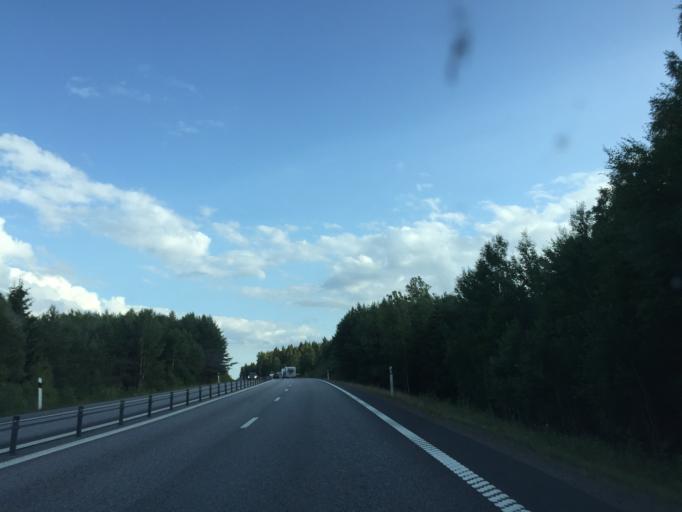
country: SE
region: OEstergoetland
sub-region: Motala Kommun
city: Motala
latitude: 58.6038
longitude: 14.9858
